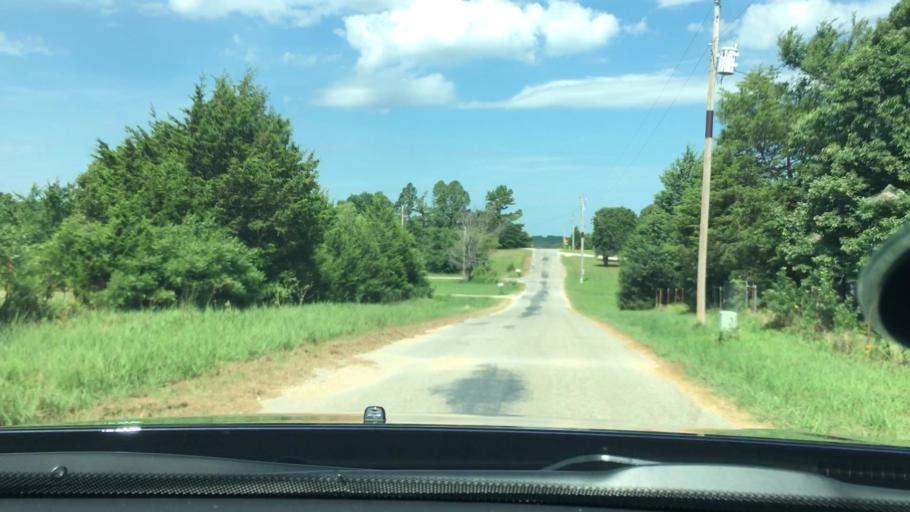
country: US
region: Oklahoma
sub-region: Pontotoc County
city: Ada
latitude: 34.7636
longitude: -96.5664
